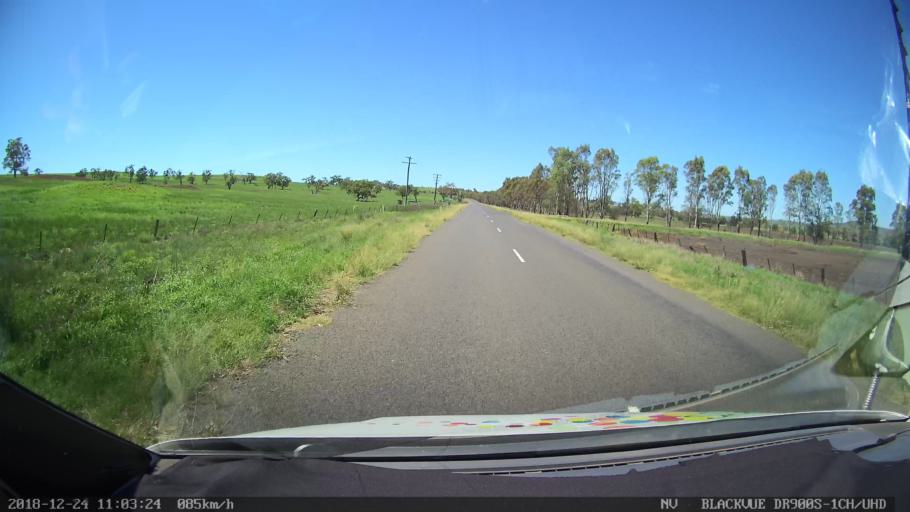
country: AU
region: New South Wales
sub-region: Upper Hunter Shire
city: Merriwa
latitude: -32.0963
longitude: 150.3688
